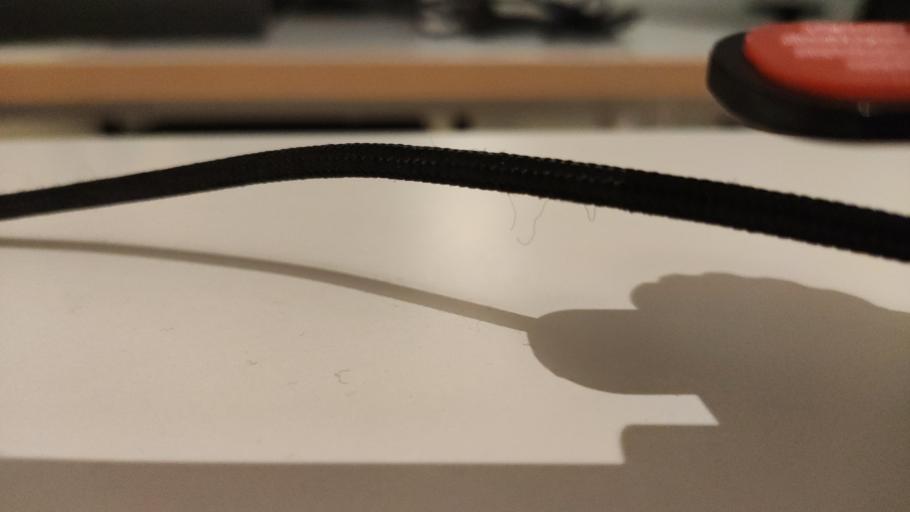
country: RU
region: Moskovskaya
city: Kurovskoye
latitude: 55.5851
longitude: 38.8922
